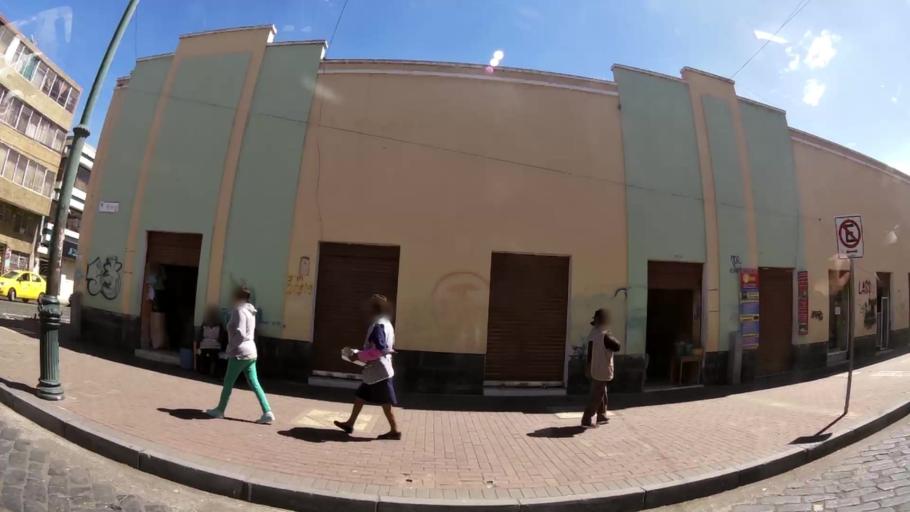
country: EC
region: Chimborazo
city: Riobamba
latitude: -1.6749
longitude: -78.6474
